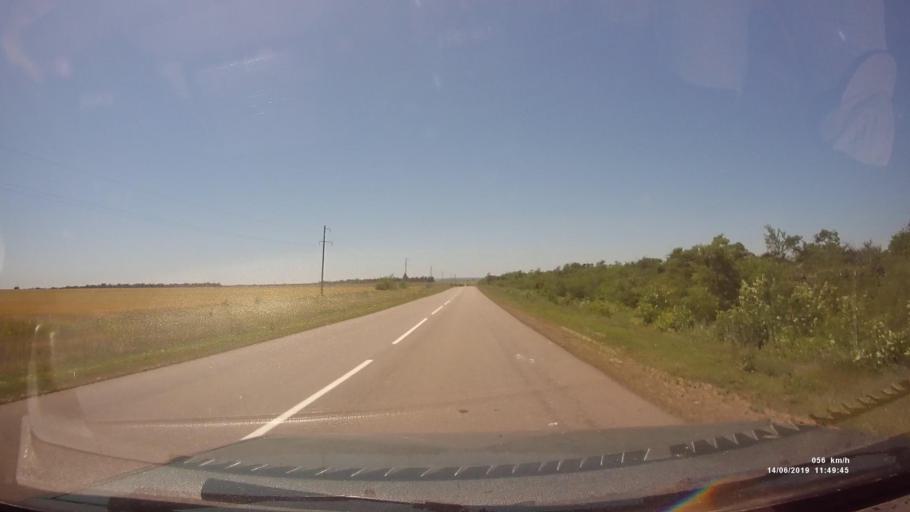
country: RU
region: Rostov
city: Kazanskaya
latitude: 49.8523
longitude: 41.2738
